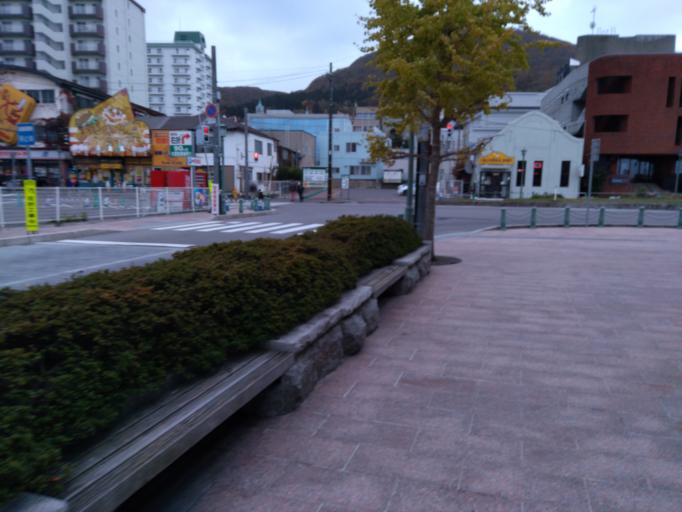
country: JP
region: Hokkaido
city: Hakodate
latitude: 41.7663
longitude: 140.7152
